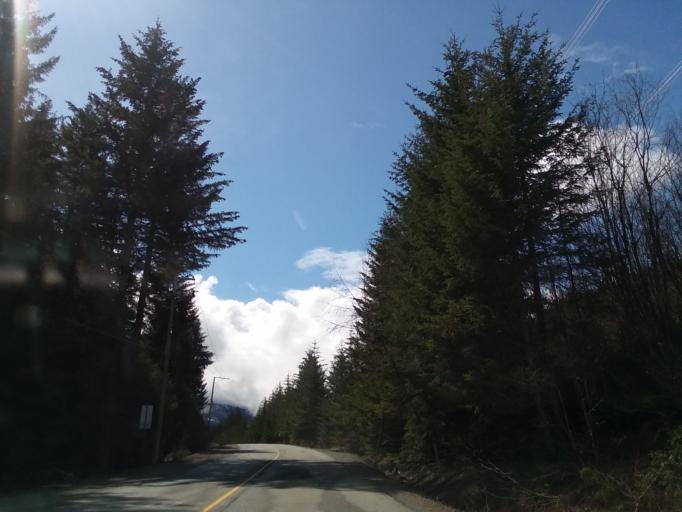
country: CA
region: British Columbia
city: Whistler
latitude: 50.1204
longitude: -122.9861
